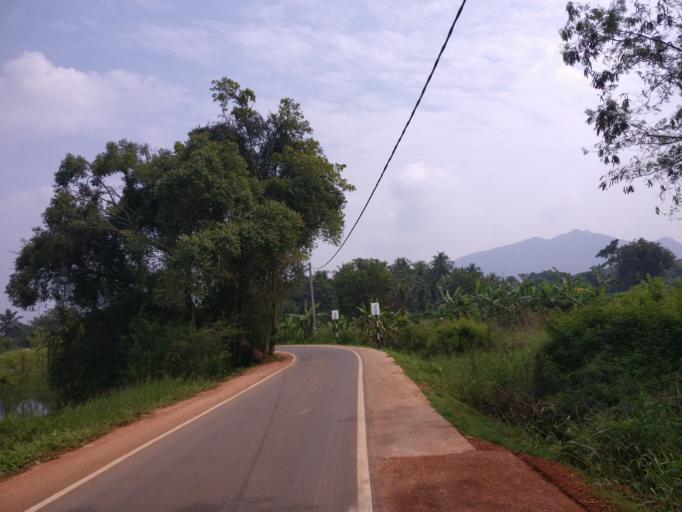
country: LK
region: Central
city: Dambulla
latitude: 7.8358
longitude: 80.6496
